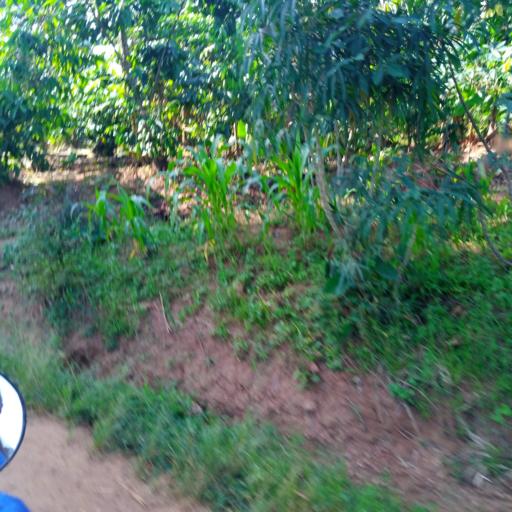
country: UG
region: Central Region
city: Masaka
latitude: -0.4375
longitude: 31.6646
